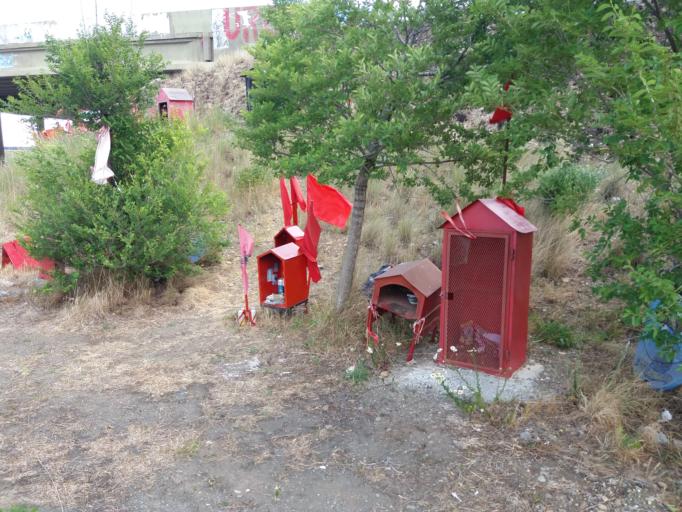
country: AR
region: Santa Cruz
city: Rio Gallegos
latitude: -51.6176
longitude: -69.2993
